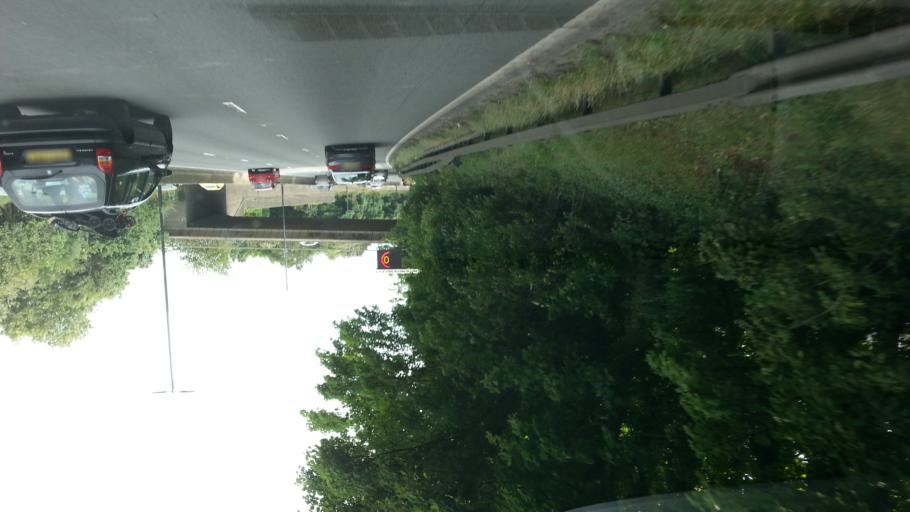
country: GB
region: Wales
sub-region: Newport
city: Newport
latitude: 51.5760
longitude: -3.0324
